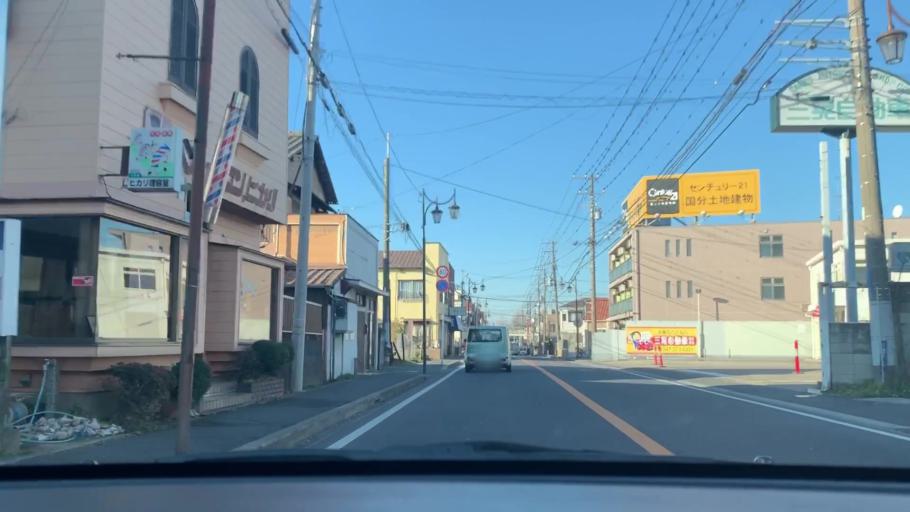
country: JP
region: Chiba
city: Matsudo
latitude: 35.7500
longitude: 139.9032
